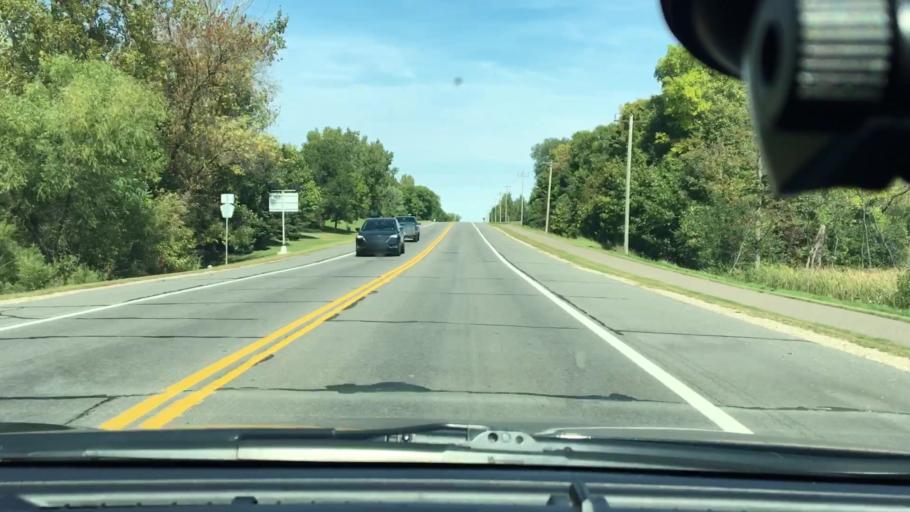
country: US
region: Minnesota
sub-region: Wright County
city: Hanover
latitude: 45.1636
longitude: -93.6659
